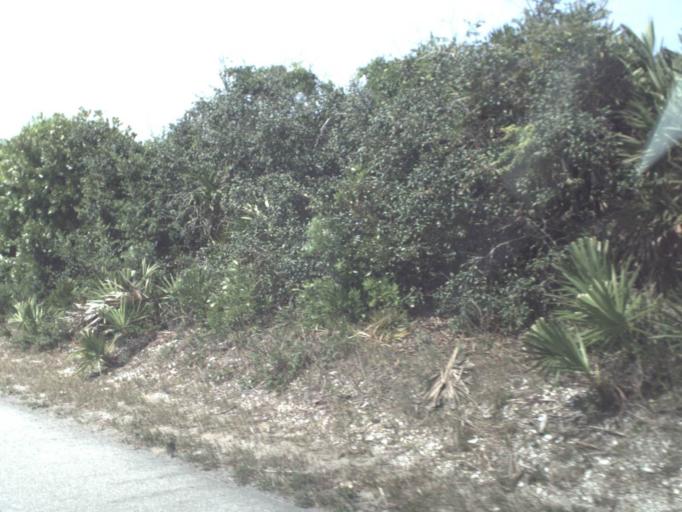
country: US
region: Florida
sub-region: Saint Johns County
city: Palm Valley
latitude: 30.1013
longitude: -81.3419
